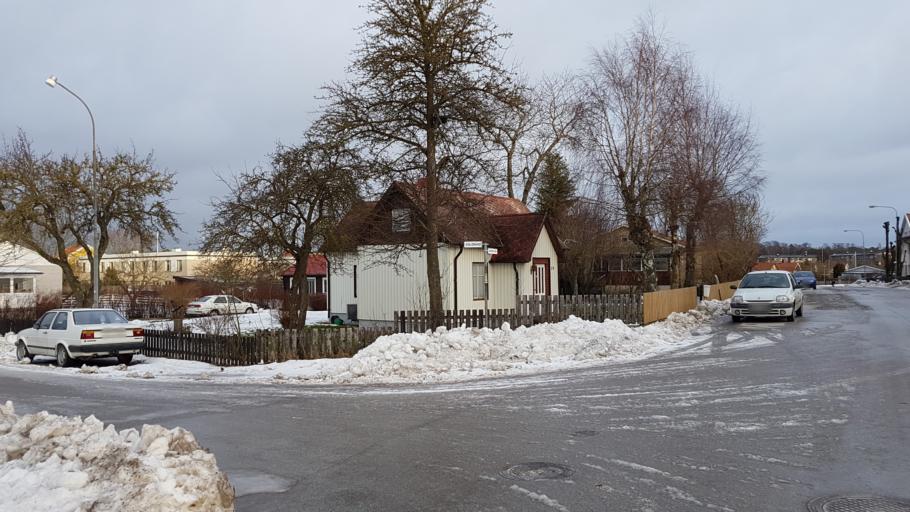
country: SE
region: Gotland
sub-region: Gotland
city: Visby
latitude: 57.6208
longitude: 18.2892
